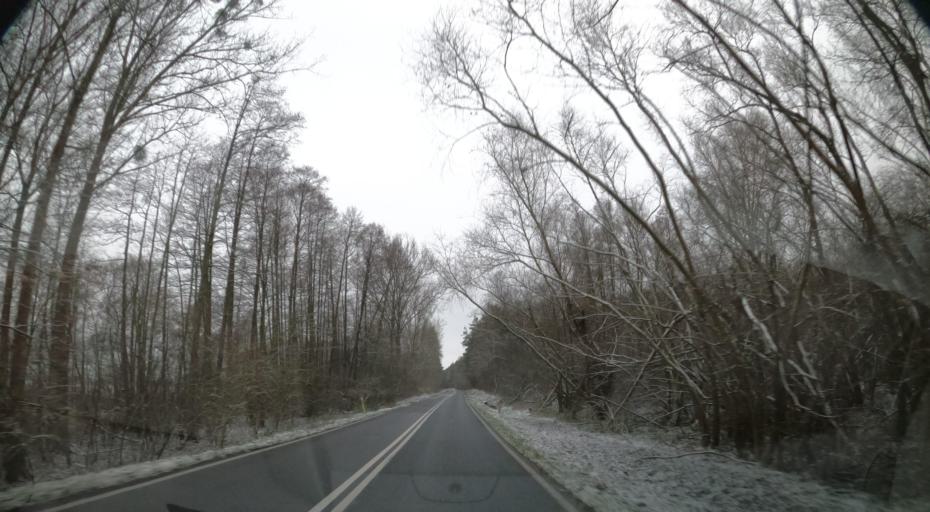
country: PL
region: Masovian Voivodeship
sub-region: Powiat plocki
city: Maszewo Duze
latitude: 52.5712
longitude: 19.5664
